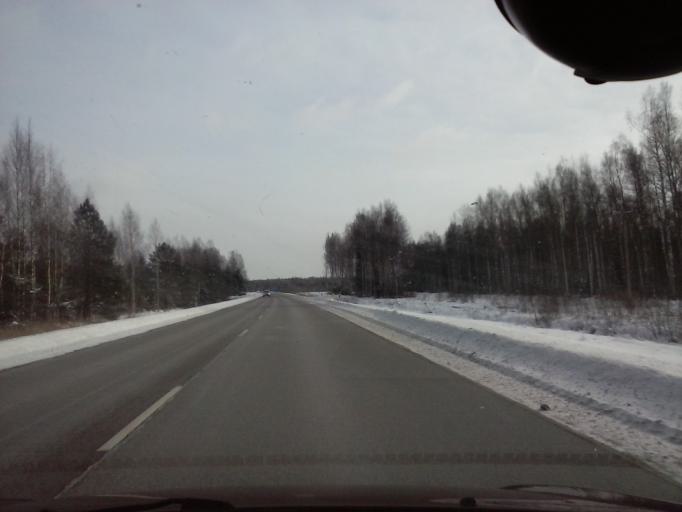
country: EE
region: Paernumaa
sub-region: Saarde vald
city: Kilingi-Nomme
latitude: 58.1745
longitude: 24.8069
